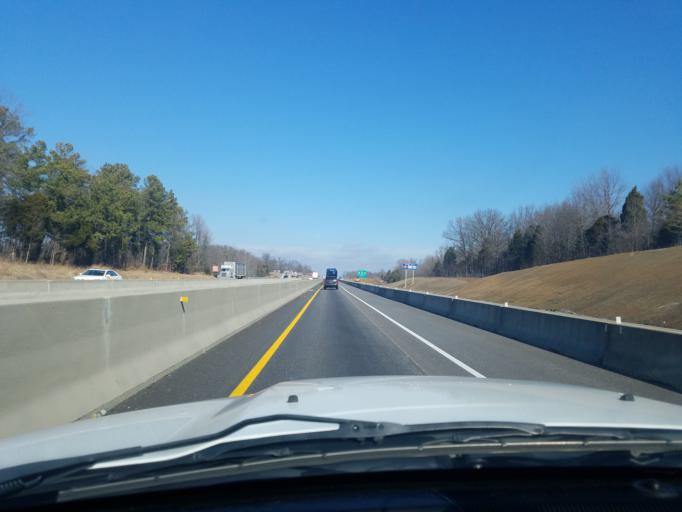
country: US
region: Kentucky
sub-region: Hardin County
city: Elizabethtown
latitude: 37.6471
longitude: -85.8576
